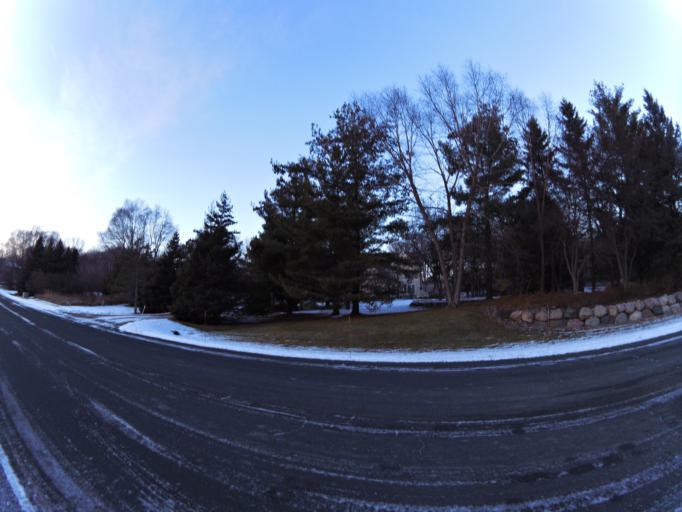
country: US
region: Minnesota
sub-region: Washington County
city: Lake Elmo
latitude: 44.9622
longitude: -92.8361
